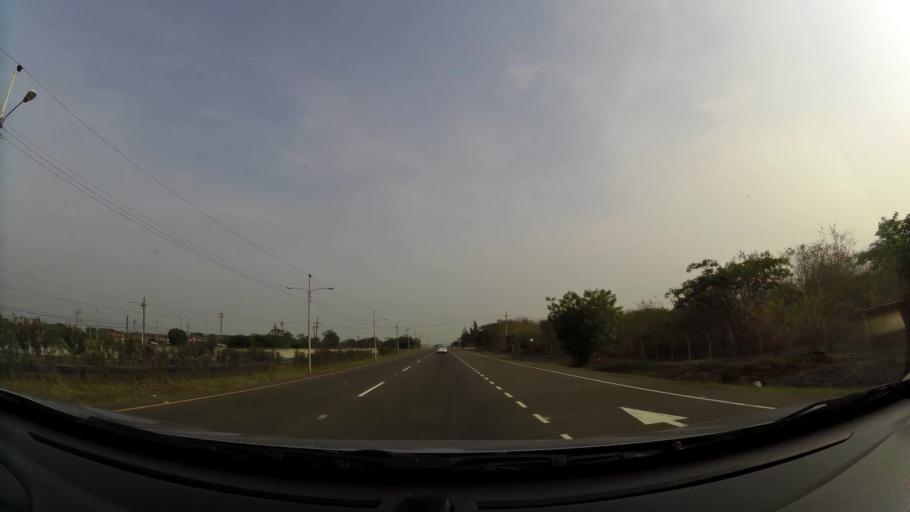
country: HN
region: La Paz
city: Yarumela
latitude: 14.3833
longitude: -87.6106
